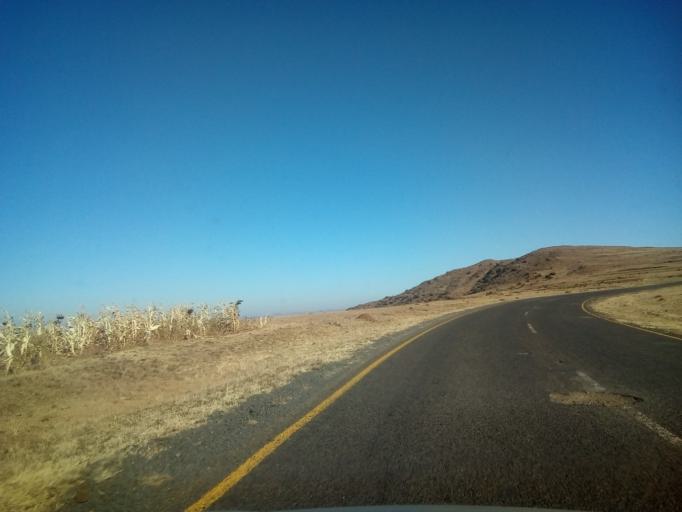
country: LS
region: Berea
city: Teyateyaneng
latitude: -29.2546
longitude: 27.7755
